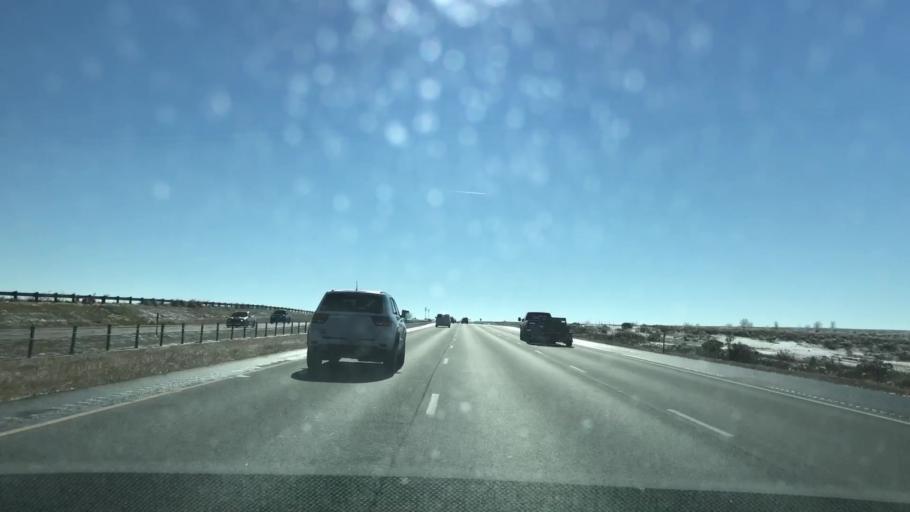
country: US
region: Colorado
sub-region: Weld County
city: Mead
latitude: 40.2867
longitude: -104.9803
